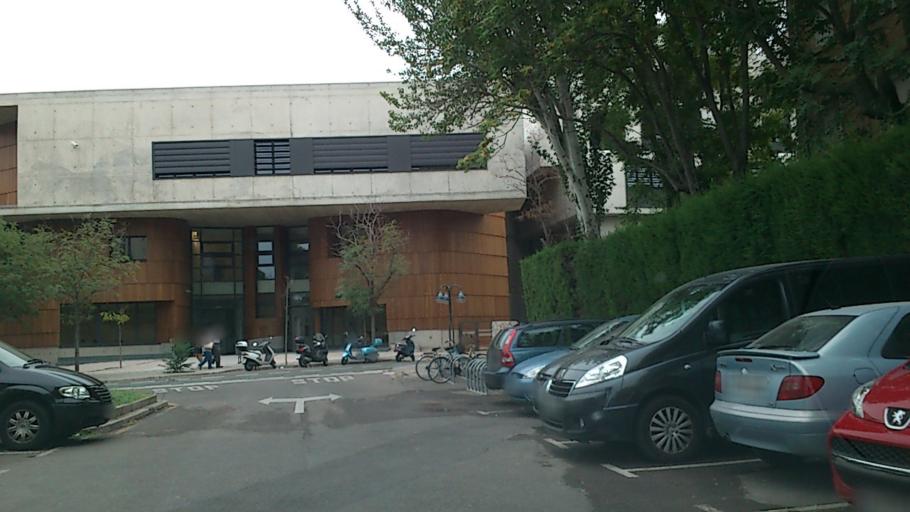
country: ES
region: Aragon
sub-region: Provincia de Zaragoza
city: Delicias
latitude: 41.6420
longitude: -0.9015
